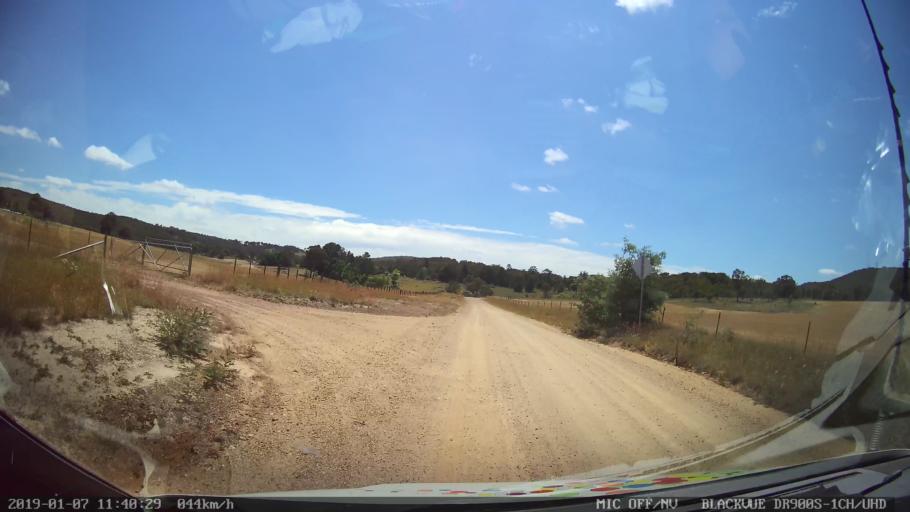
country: AU
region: New South Wales
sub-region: Armidale Dumaresq
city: Armidale
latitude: -30.3638
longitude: 151.5842
